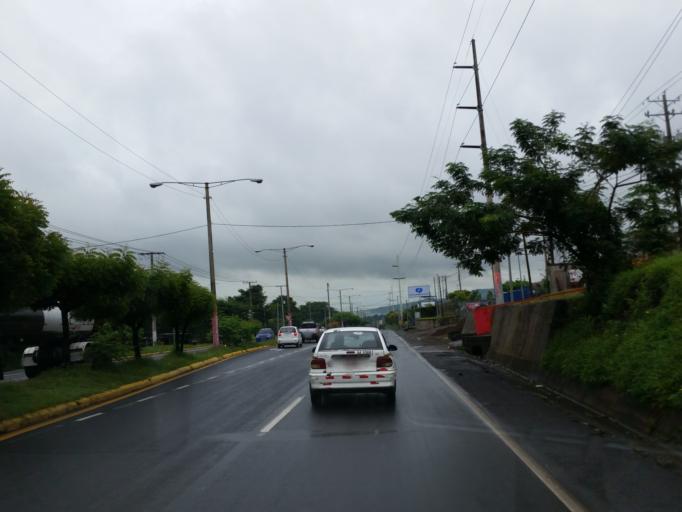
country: NI
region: Managua
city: Ciudad Sandino
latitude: 12.1571
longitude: -86.3383
